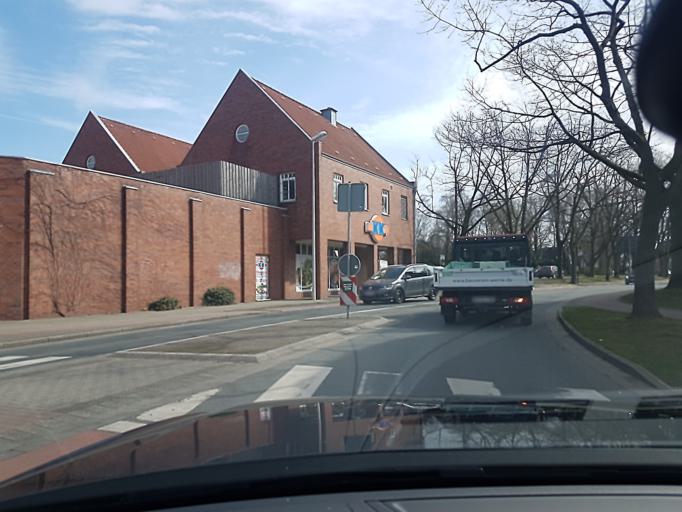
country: DE
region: North Rhine-Westphalia
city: Werne
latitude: 51.6611
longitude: 7.6327
